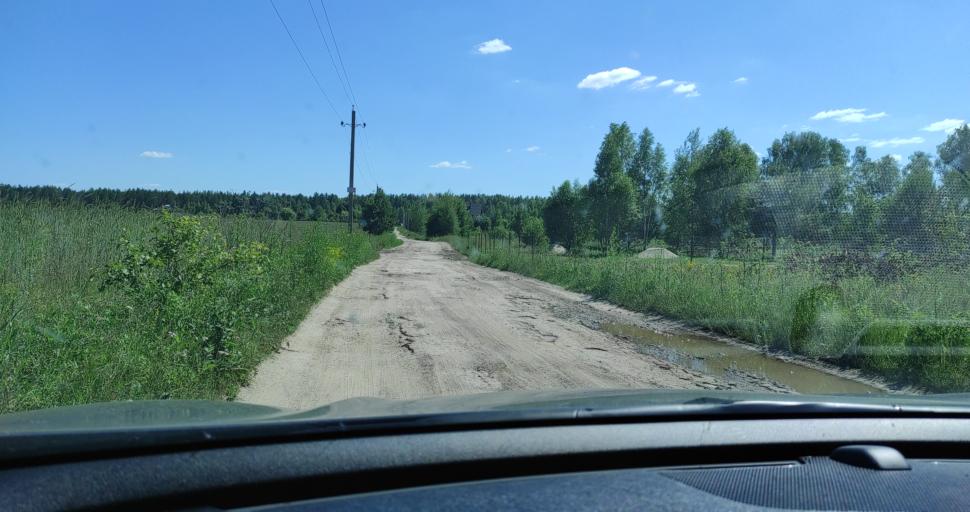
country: RU
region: Rjazan
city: Murmino
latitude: 54.5653
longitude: 40.0967
